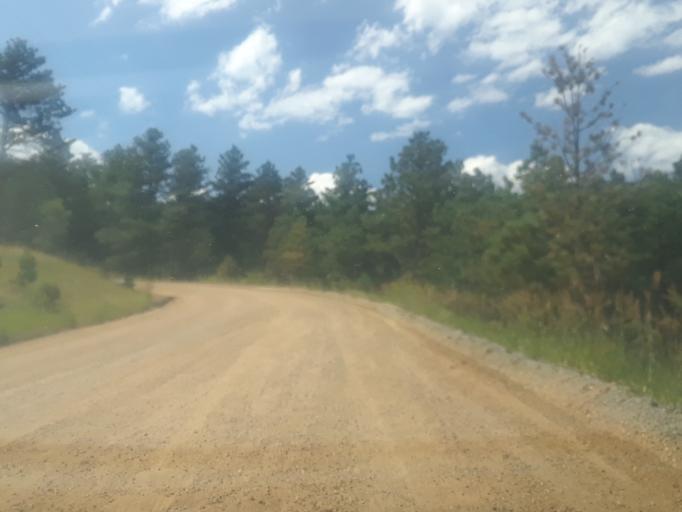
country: US
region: Colorado
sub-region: Boulder County
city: Boulder
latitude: 40.0611
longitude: -105.3716
